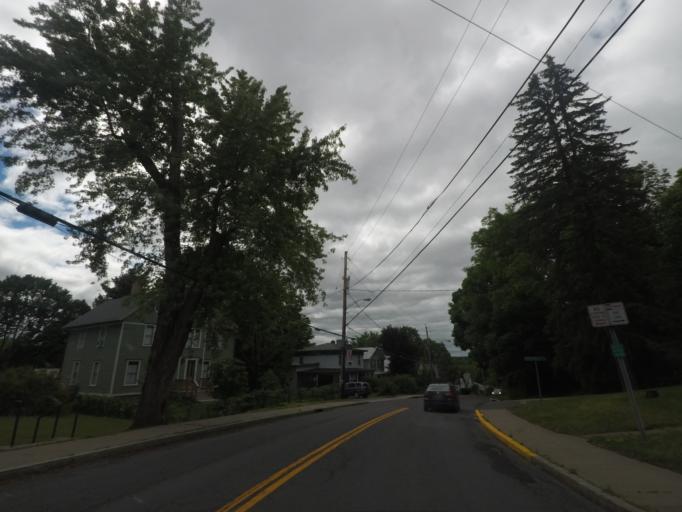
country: US
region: New York
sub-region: Columbia County
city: Philmont
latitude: 42.2477
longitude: -73.6533
